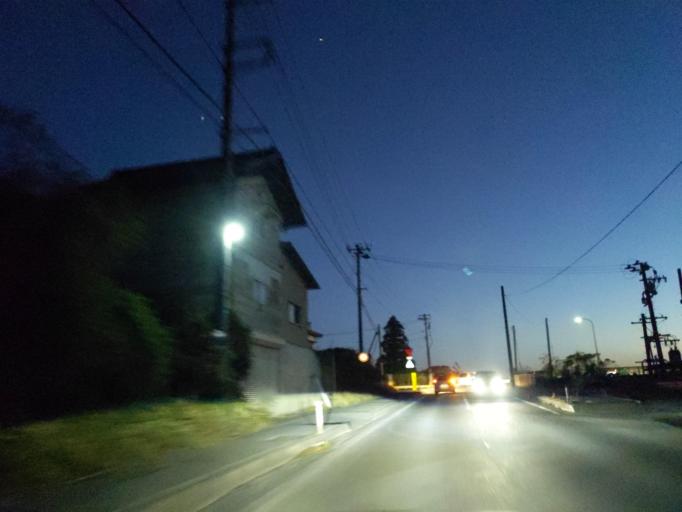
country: JP
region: Fukushima
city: Sukagawa
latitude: 37.3083
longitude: 140.3814
